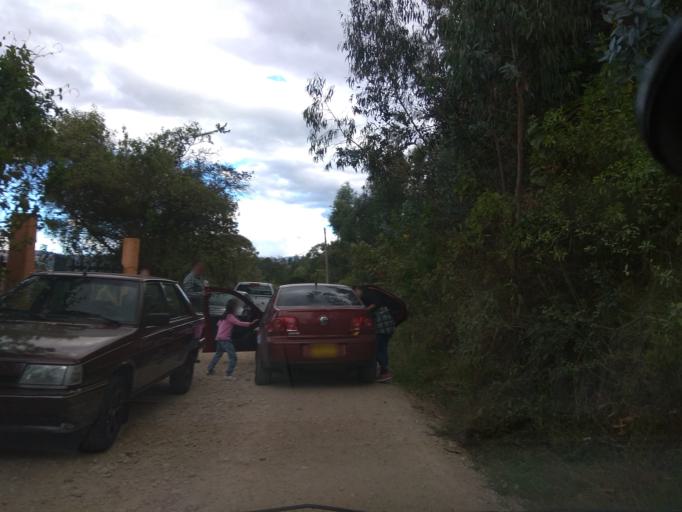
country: CO
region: Boyaca
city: Paipa
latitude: 5.7981
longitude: -73.1106
